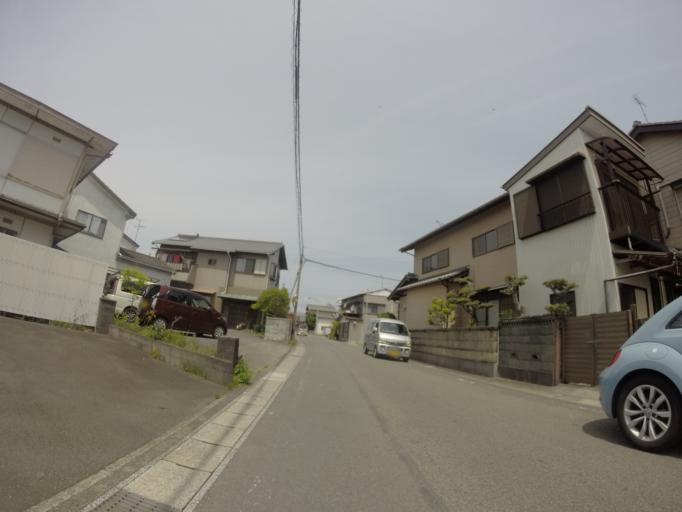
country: JP
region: Shizuoka
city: Yaizu
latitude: 34.8432
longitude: 138.3297
